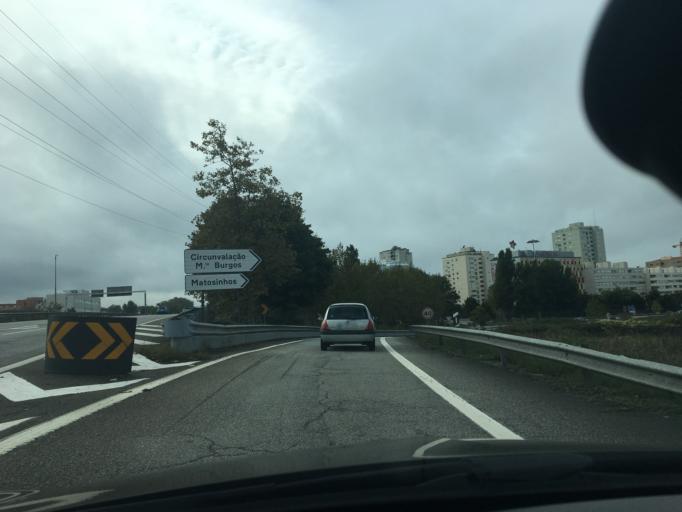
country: PT
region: Porto
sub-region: Matosinhos
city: Sao Mamede de Infesta
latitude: 41.1814
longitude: -8.6225
